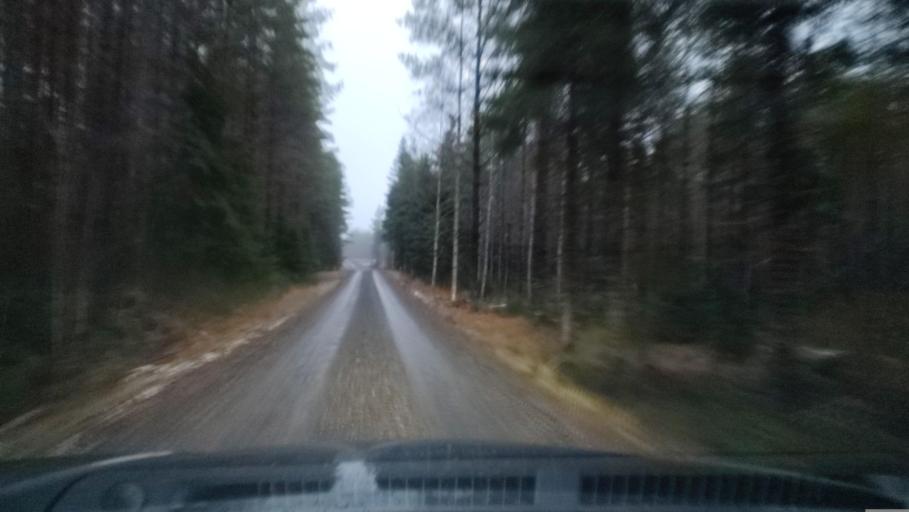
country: FI
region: Southern Ostrobothnia
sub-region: Suupohja
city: Karijoki
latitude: 62.1424
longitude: 21.6272
